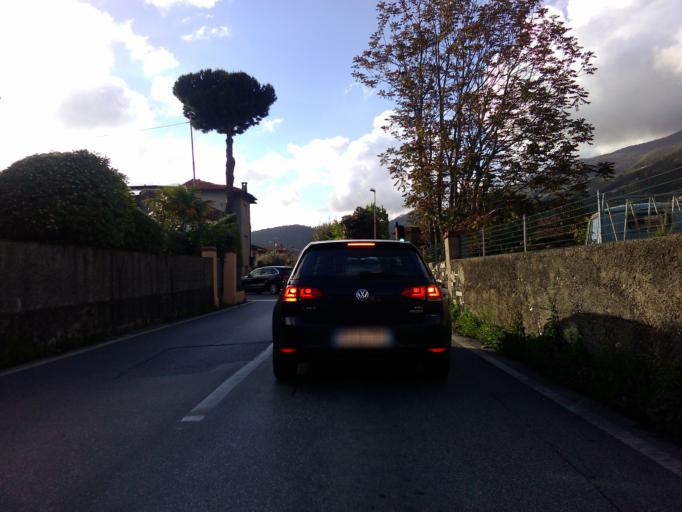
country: IT
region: Tuscany
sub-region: Provincia di Lucca
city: Ripa-Pozzi-Querceta-Ponterosso
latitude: 43.9836
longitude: 10.2107
